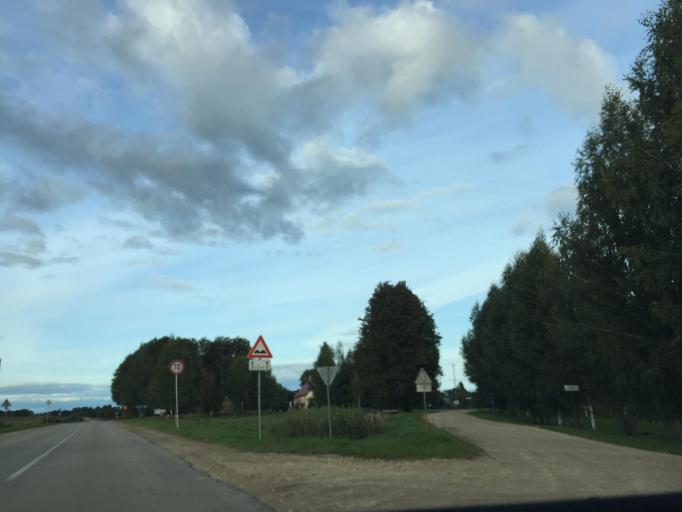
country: LV
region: Nereta
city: Nereta
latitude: 56.2824
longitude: 25.3998
